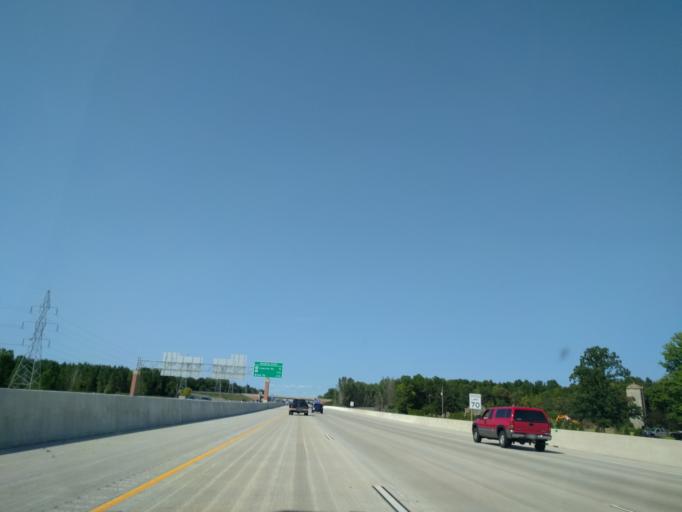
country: US
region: Wisconsin
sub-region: Brown County
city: Howard
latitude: 44.5725
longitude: -88.0484
